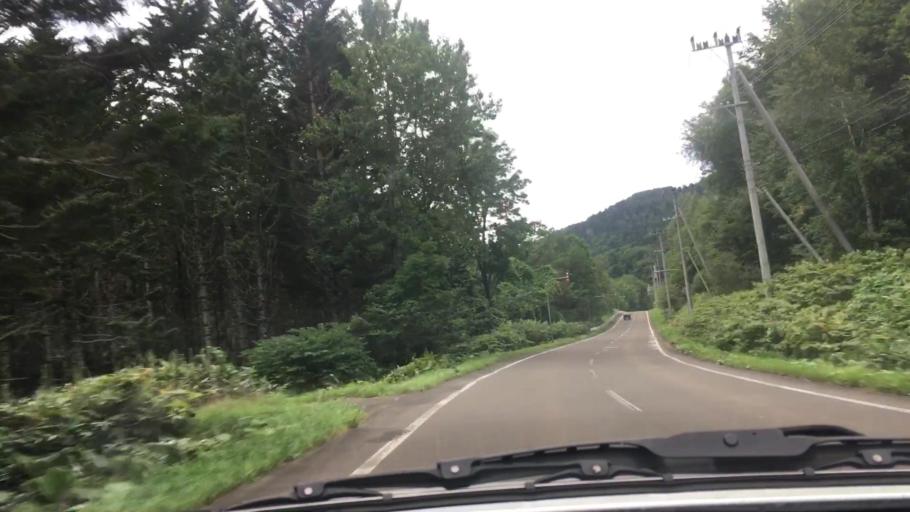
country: JP
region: Hokkaido
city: Shimo-furano
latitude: 43.0444
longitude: 142.5183
